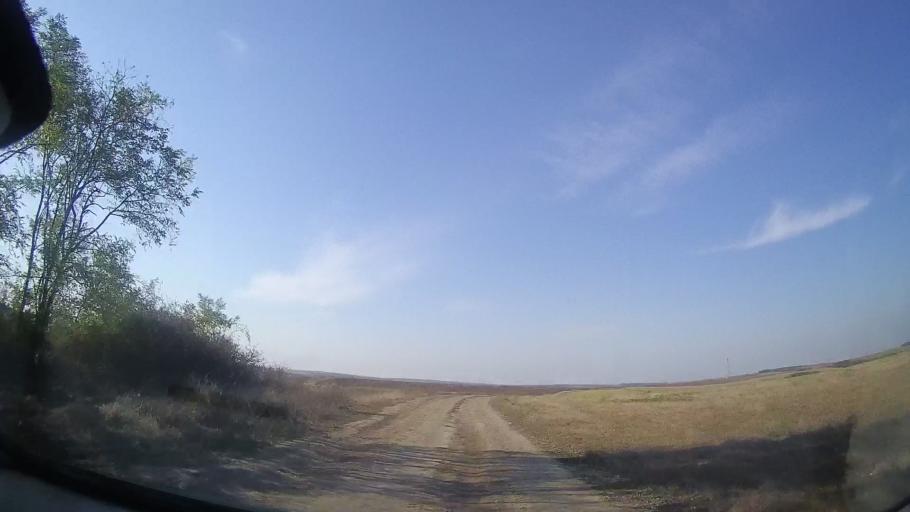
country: RO
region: Timis
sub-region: Comuna Bogda
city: Bogda
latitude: 45.8850
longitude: 21.5561
